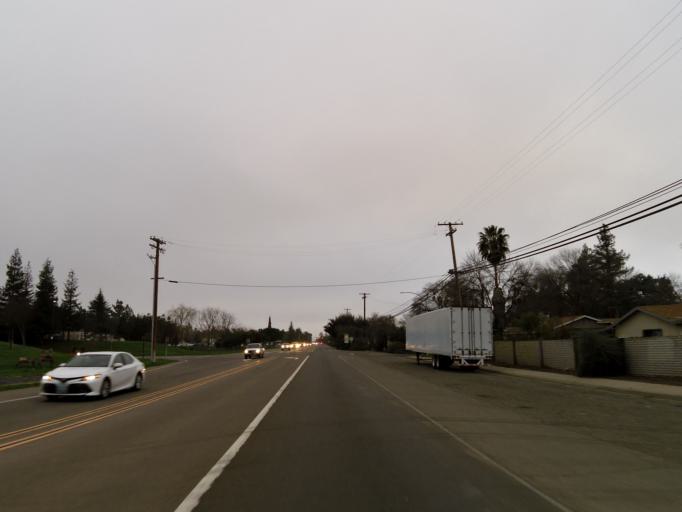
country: US
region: California
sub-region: Stanislaus County
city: West Modesto
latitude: 37.6387
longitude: -121.0245
